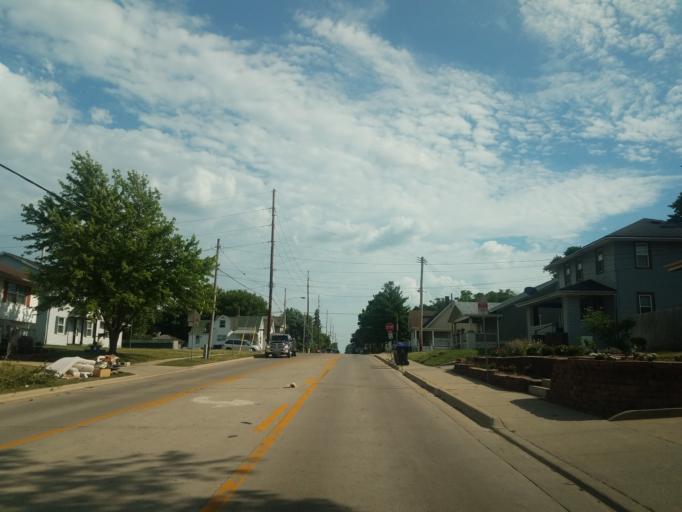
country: US
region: Illinois
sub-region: McLean County
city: Bloomington
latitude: 40.4740
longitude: -89.0065
